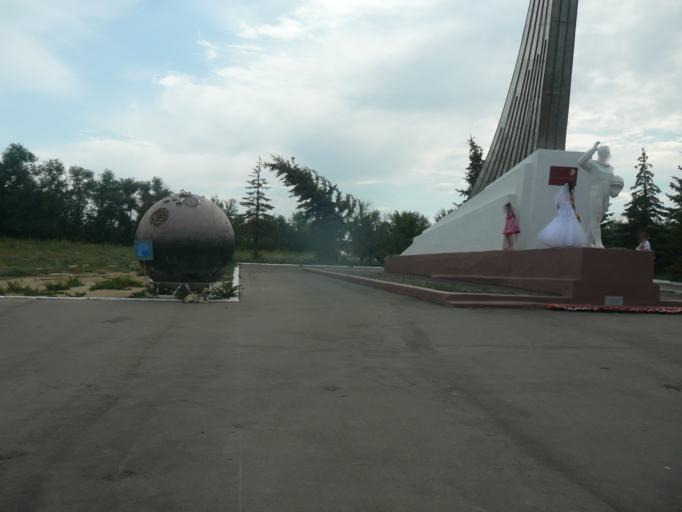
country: RU
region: Saratov
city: Privolzhskiy
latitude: 51.2708
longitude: 45.9974
